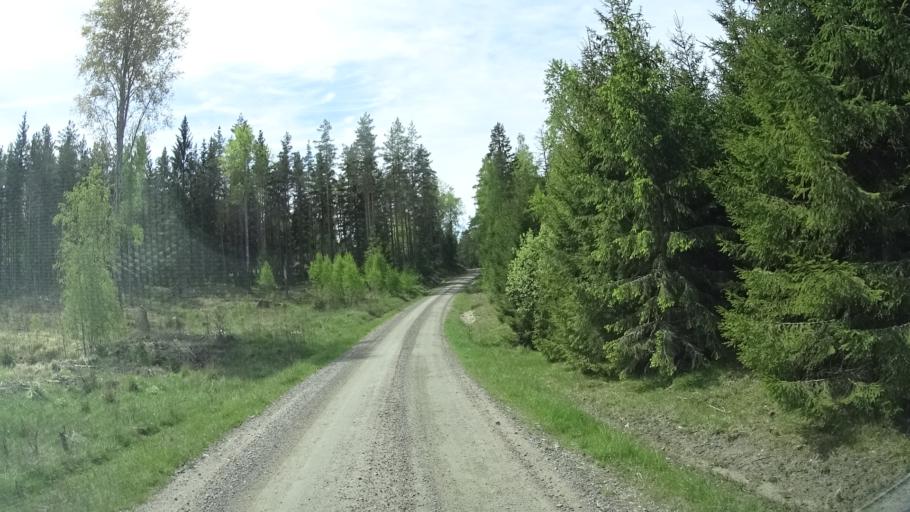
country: SE
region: OEstergoetland
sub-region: Finspangs Kommun
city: Finspang
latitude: 58.7702
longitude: 15.8482
